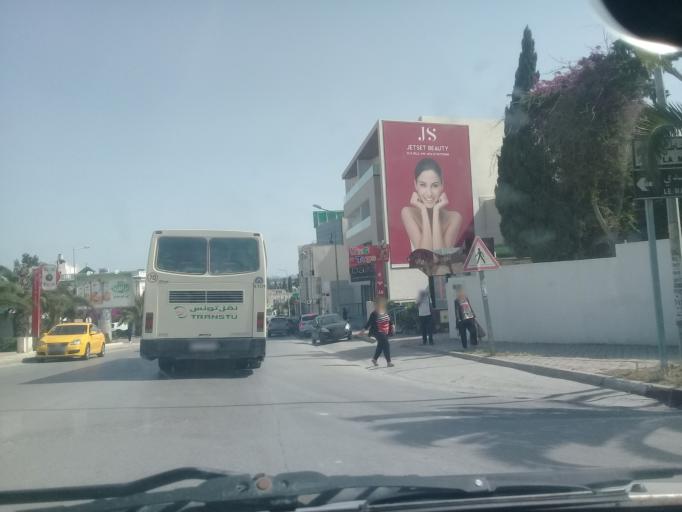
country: TN
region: Tunis
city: Al Marsa
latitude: 36.8887
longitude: 10.3224
